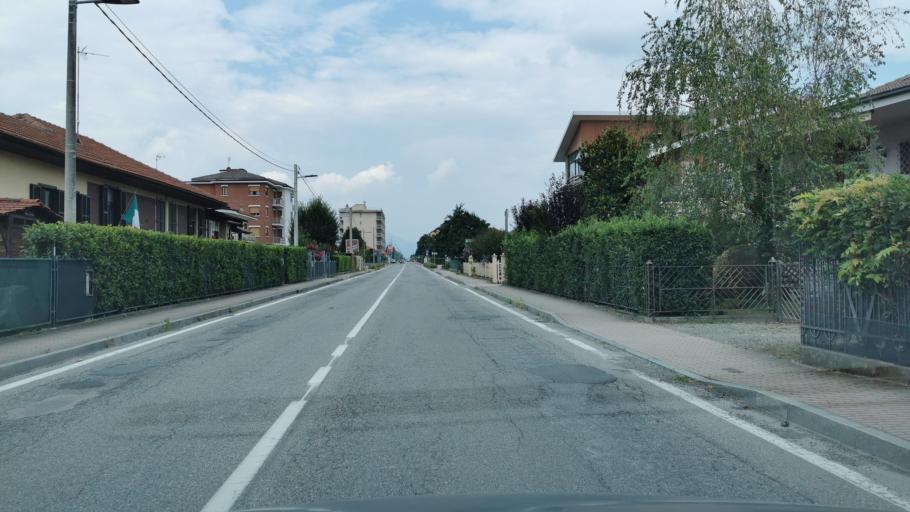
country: IT
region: Piedmont
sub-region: Provincia di Torino
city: Cavour
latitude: 44.7893
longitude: 7.3755
